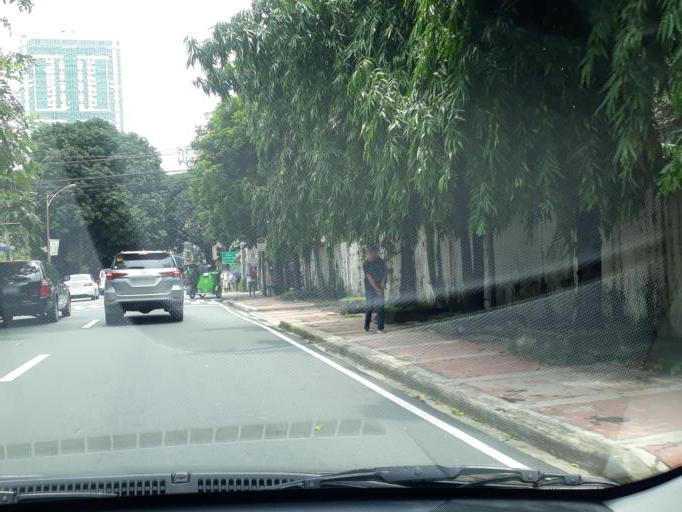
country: PH
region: Metro Manila
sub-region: San Juan
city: San Juan
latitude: 14.6149
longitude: 121.0340
